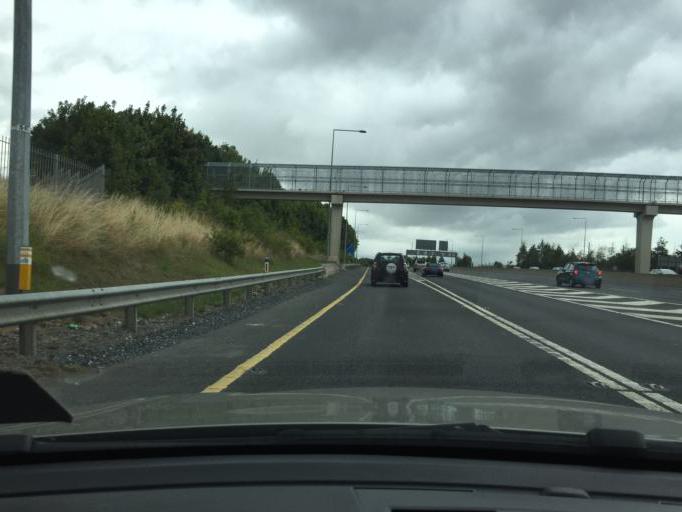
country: IE
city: Knocklyon
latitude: 53.2933
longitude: -6.3328
